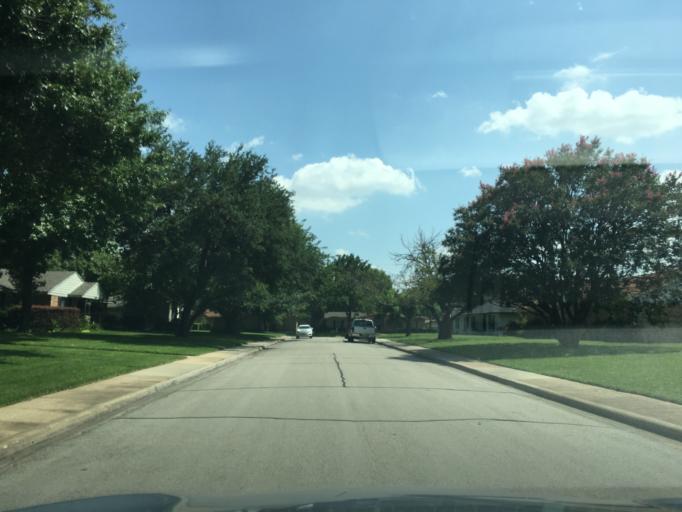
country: US
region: Texas
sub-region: Dallas County
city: Farmers Branch
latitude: 32.9220
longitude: -96.8610
